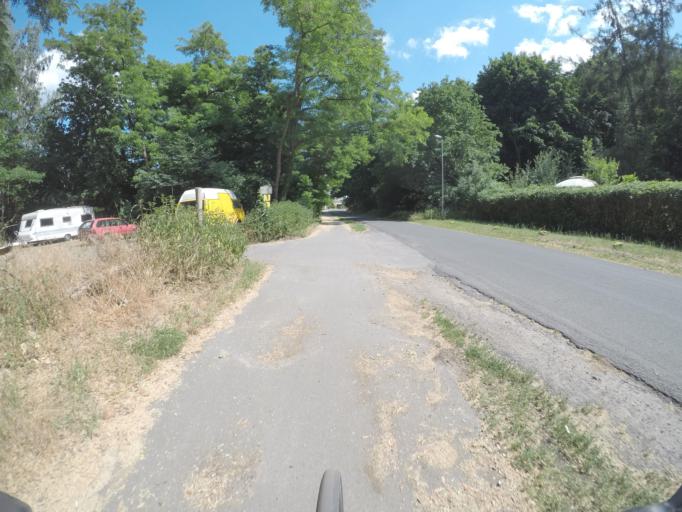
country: DE
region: Brandenburg
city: Roskow
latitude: 52.4437
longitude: 12.7325
